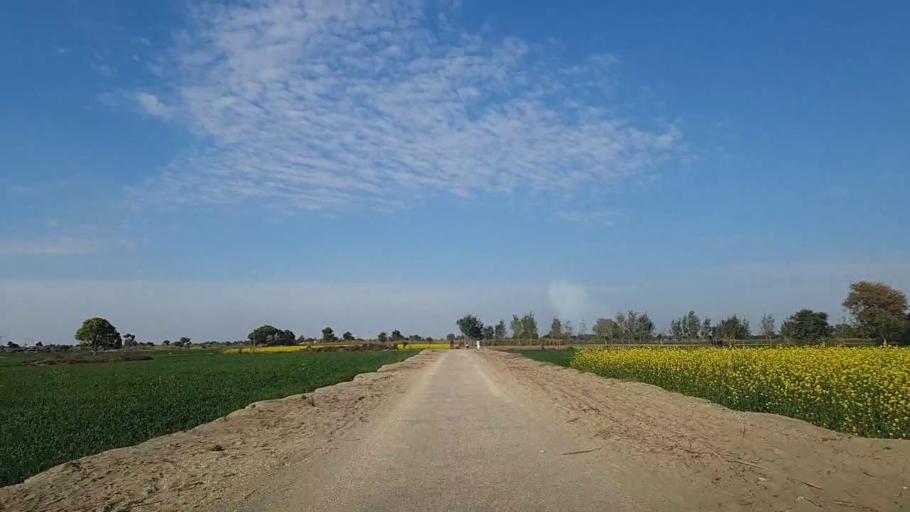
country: PK
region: Sindh
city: Khadro
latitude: 26.3068
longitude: 68.8343
